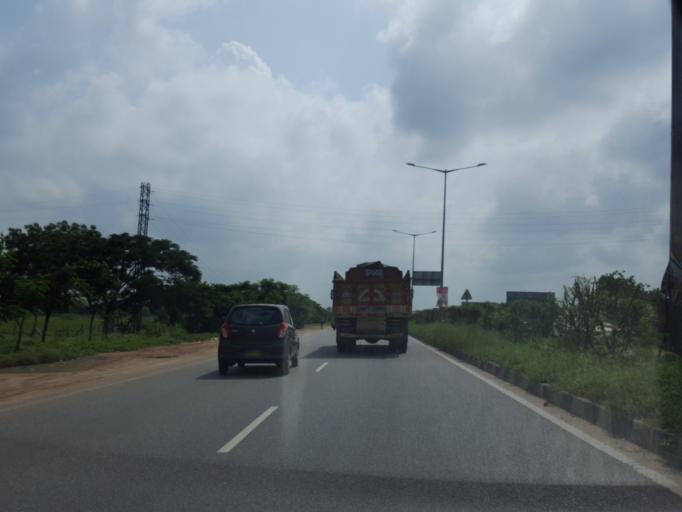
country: IN
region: Telangana
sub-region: Nalgonda
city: Bhongir
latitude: 17.2318
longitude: 78.9641
